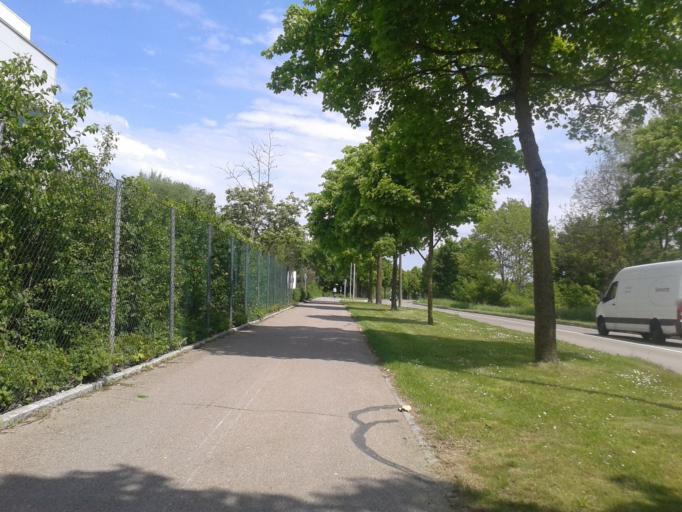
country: DE
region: Baden-Wuerttemberg
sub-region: Tuebingen Region
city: Ulm
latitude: 48.3595
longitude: 9.9518
